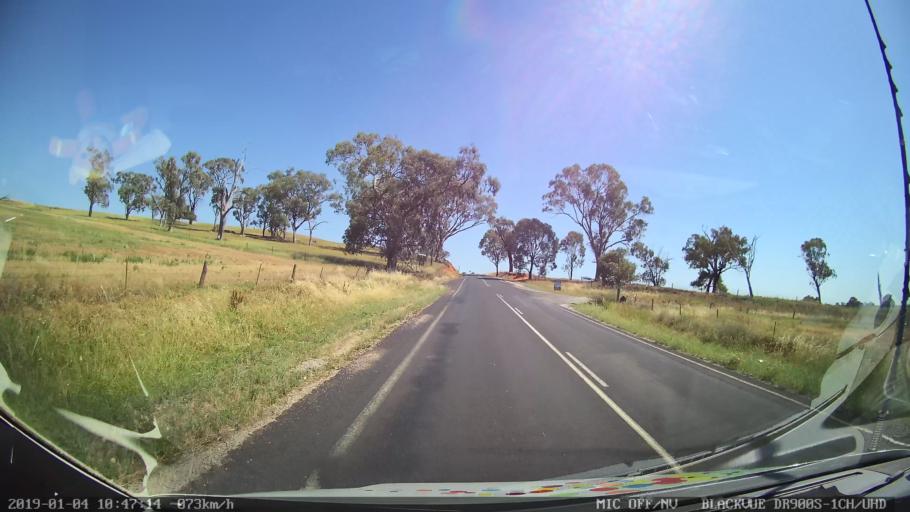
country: AU
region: New South Wales
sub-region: Cabonne
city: Molong
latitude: -33.2720
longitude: 148.7201
